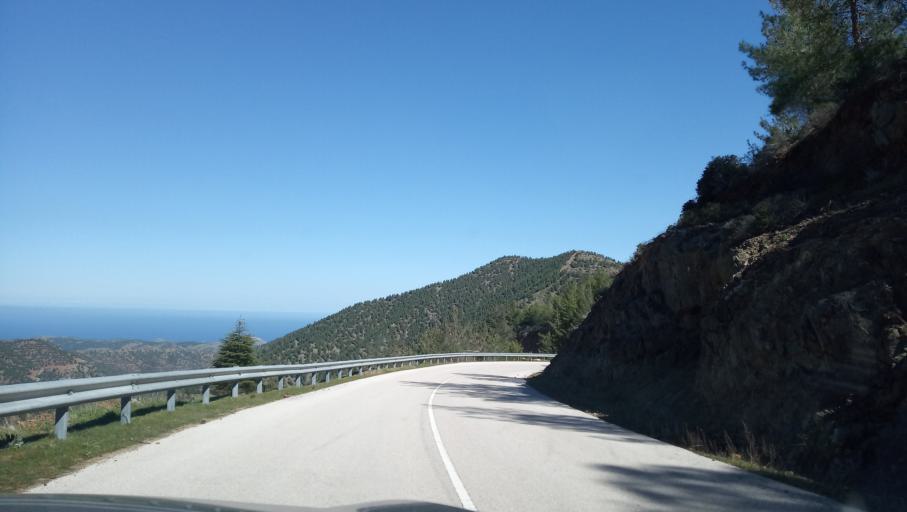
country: CY
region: Lefkosia
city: Lefka
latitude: 35.0717
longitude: 32.7624
